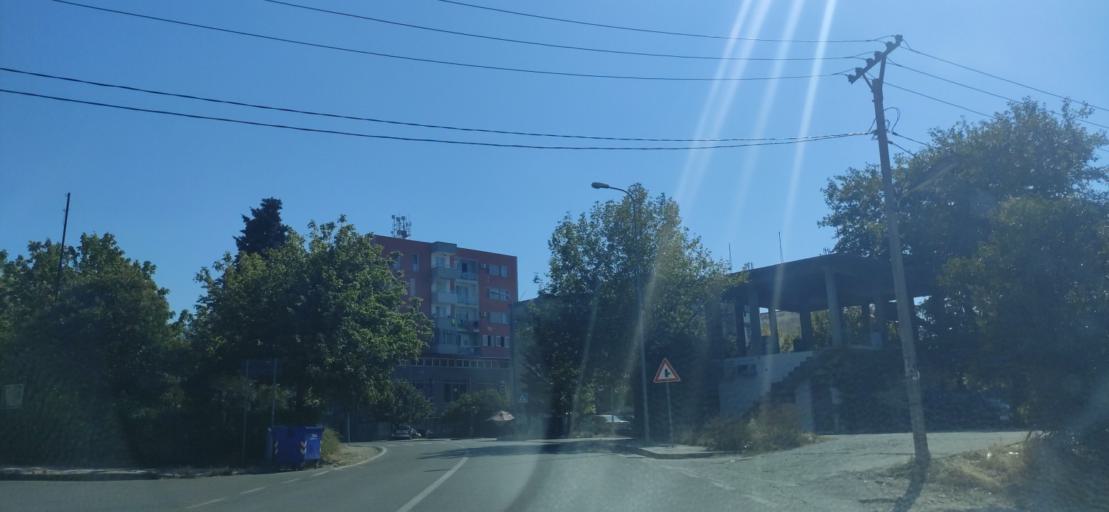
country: AL
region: Lezhe
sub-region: Rrethi i Kurbinit
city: Lac
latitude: 41.6382
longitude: 19.7119
